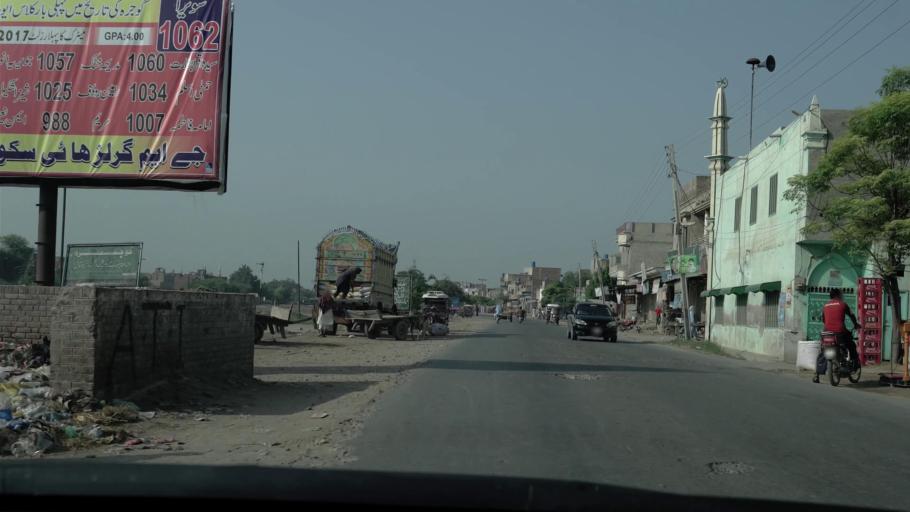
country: PK
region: Punjab
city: Gojra
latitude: 31.1266
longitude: 72.6728
